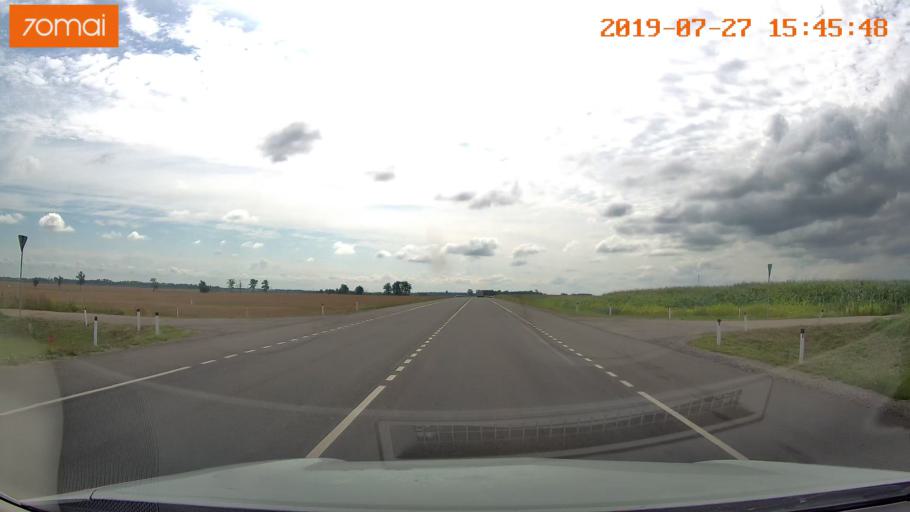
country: RU
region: Kaliningrad
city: Gusev
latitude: 54.6087
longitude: 22.1299
